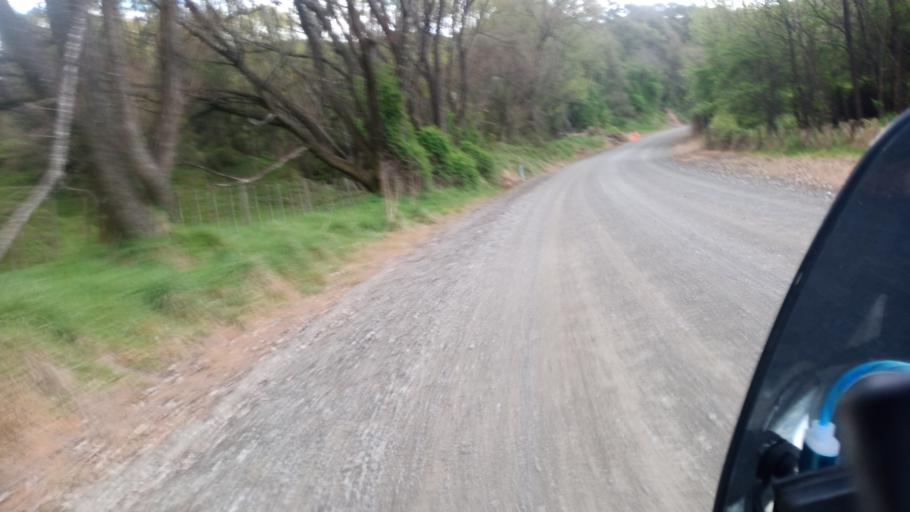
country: NZ
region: Gisborne
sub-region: Gisborne District
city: Gisborne
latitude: -38.2051
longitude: 178.2496
